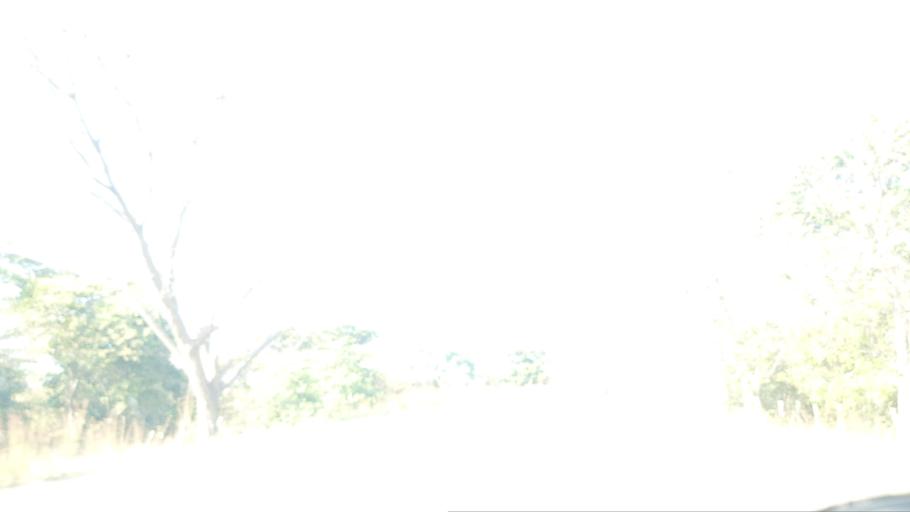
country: CO
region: Casanare
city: Municipio Hato Corozal
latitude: 6.1376
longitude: -71.7813
